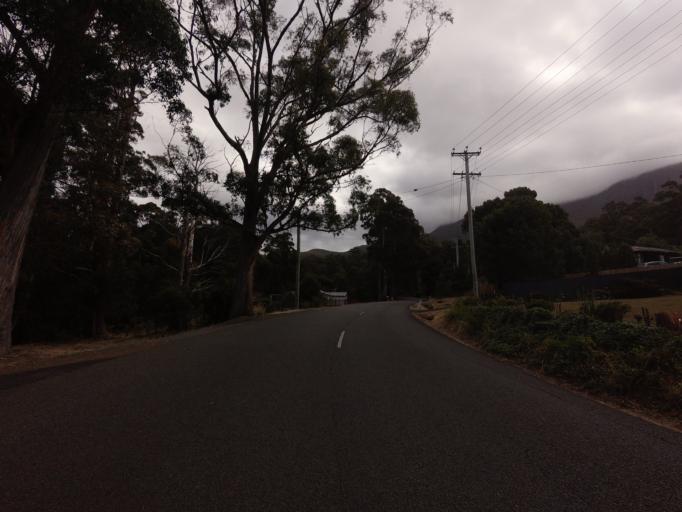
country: AU
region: Tasmania
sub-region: Hobart
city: Dynnyrne
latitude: -42.9039
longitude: 147.2706
